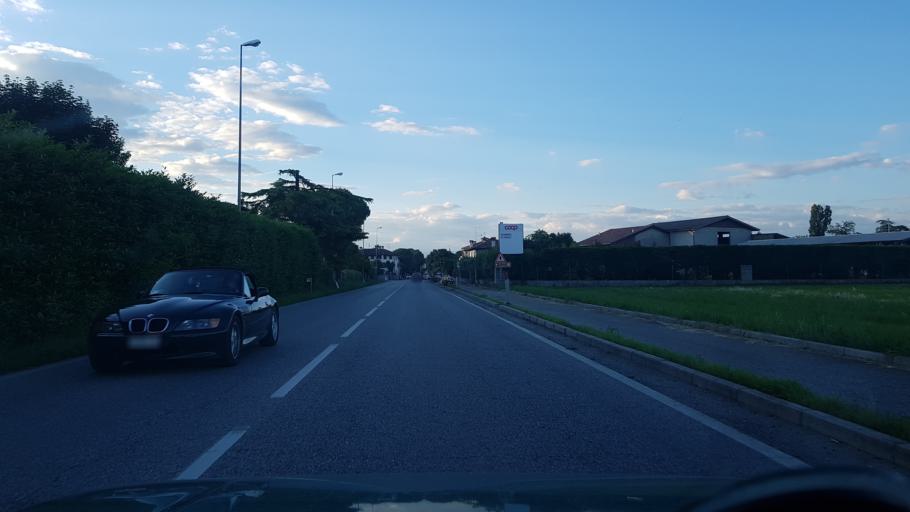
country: IT
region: Friuli Venezia Giulia
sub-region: Provincia di Udine
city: Santa Maria la Longa
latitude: 45.9190
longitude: 13.2944
